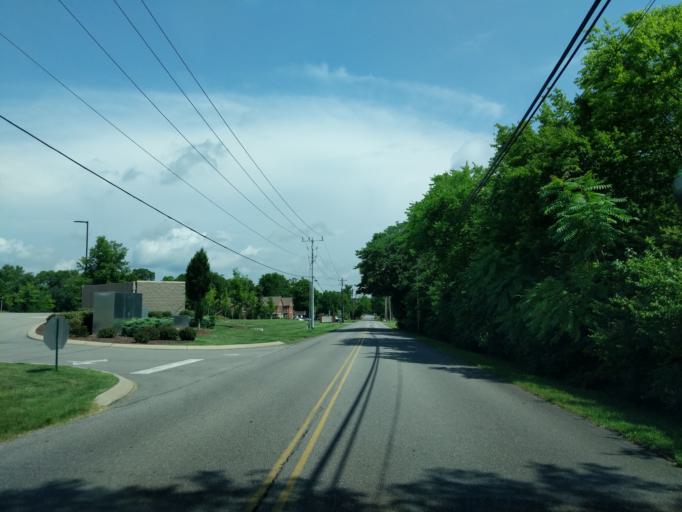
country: US
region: Tennessee
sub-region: Davidson County
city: Goodlettsville
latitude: 36.3138
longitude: -86.7066
